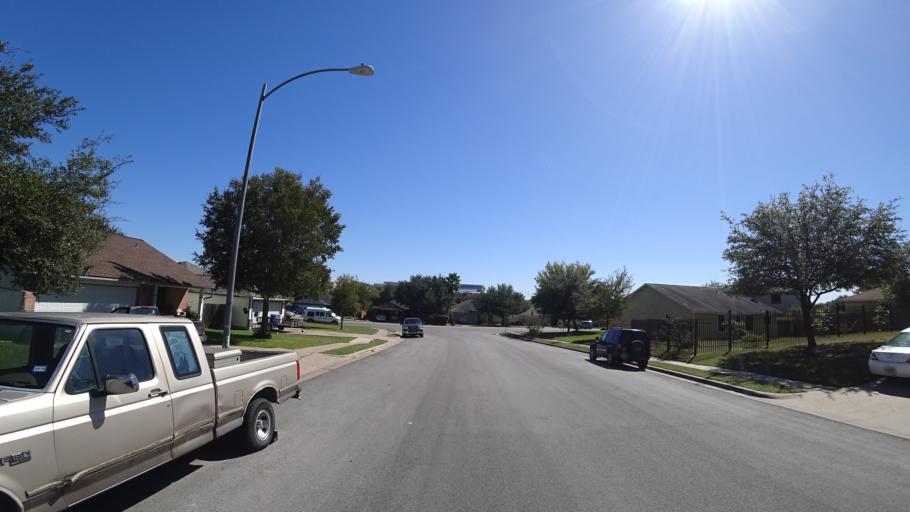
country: US
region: Texas
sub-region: Travis County
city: Hornsby Bend
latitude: 30.3026
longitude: -97.6382
